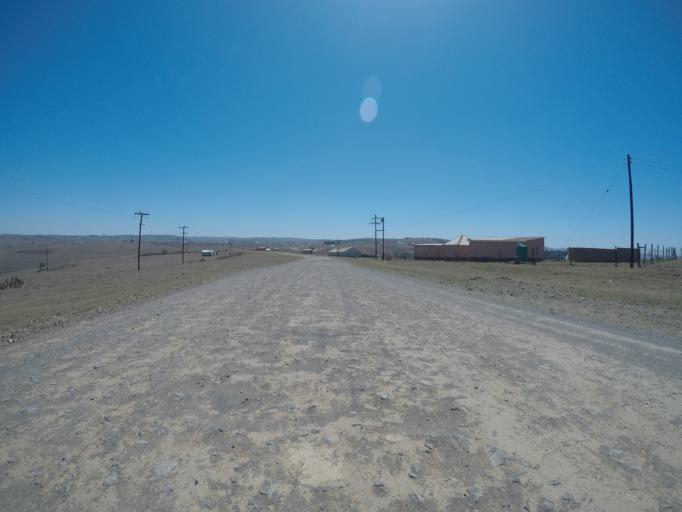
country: ZA
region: Eastern Cape
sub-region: OR Tambo District Municipality
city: Mthatha
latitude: -31.7914
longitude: 28.8231
